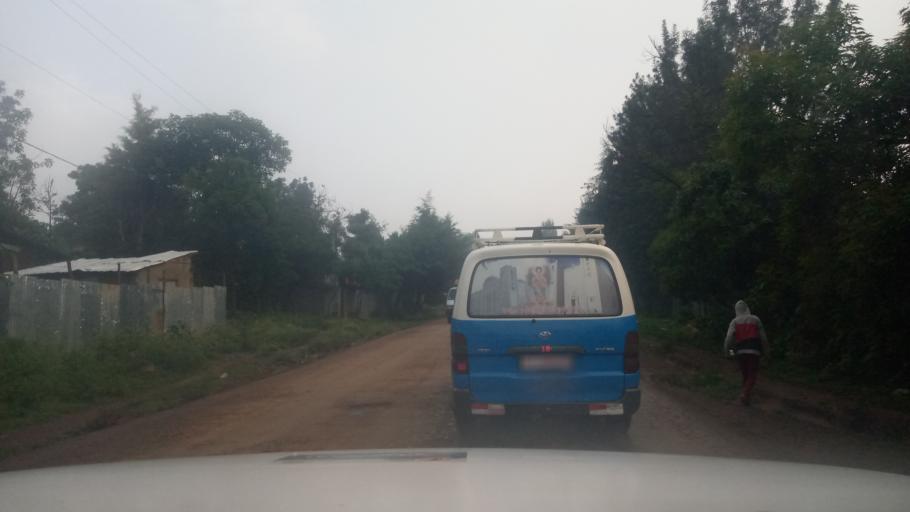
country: ET
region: Oromiya
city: Jima
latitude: 7.6962
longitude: 36.8167
